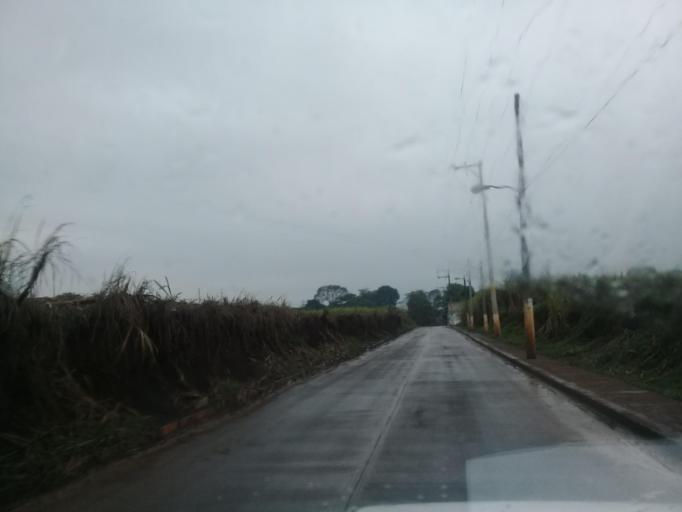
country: MX
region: Veracruz
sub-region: Cordoba
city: San Jose de Tapia
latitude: 18.8493
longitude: -96.9553
